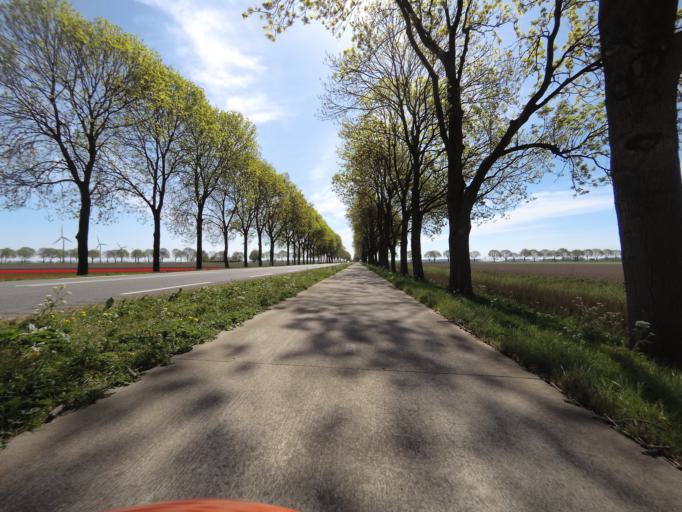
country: NL
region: Flevoland
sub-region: Gemeente Dronten
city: Biddinghuizen
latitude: 52.4852
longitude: 5.6615
